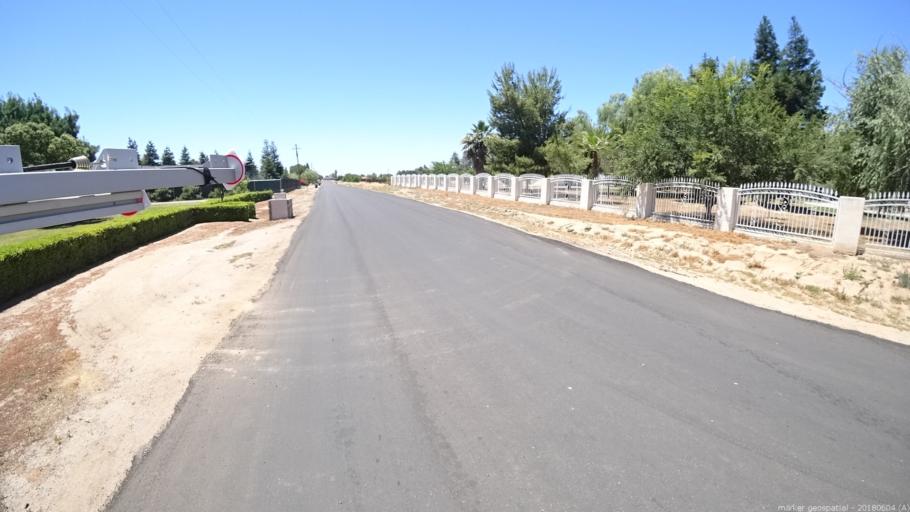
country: US
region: California
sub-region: Madera County
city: Madera Acres
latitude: 36.9936
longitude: -120.0851
